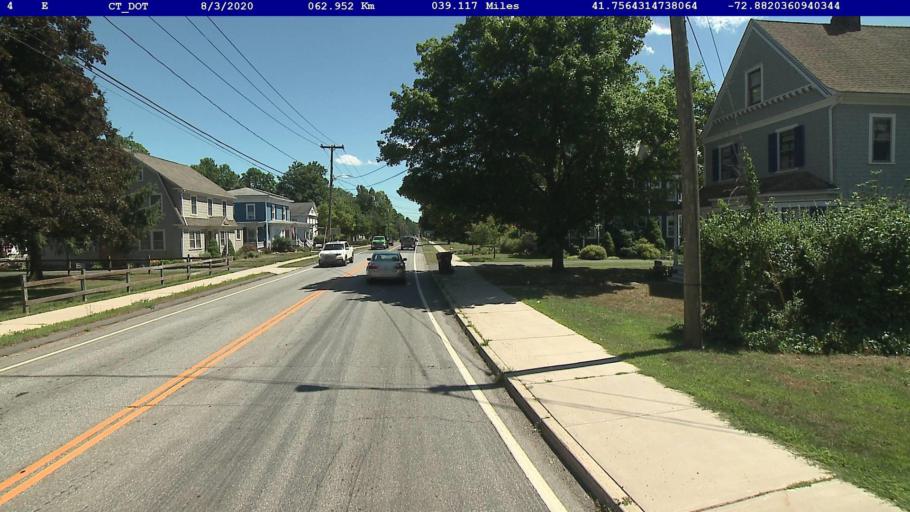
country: US
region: Connecticut
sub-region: Hartford County
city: Farmington
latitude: 41.7564
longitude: -72.8820
